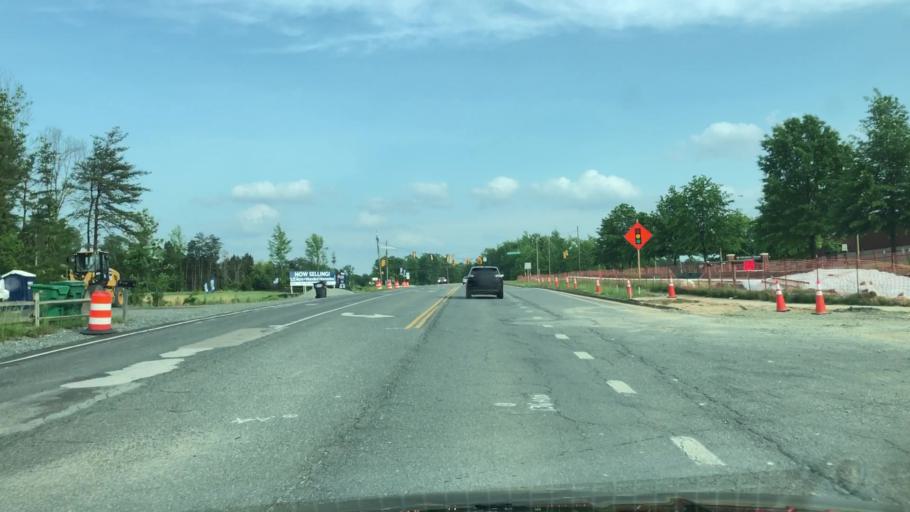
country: US
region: Virginia
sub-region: Stafford County
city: Stafford
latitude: 38.4364
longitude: -77.4509
